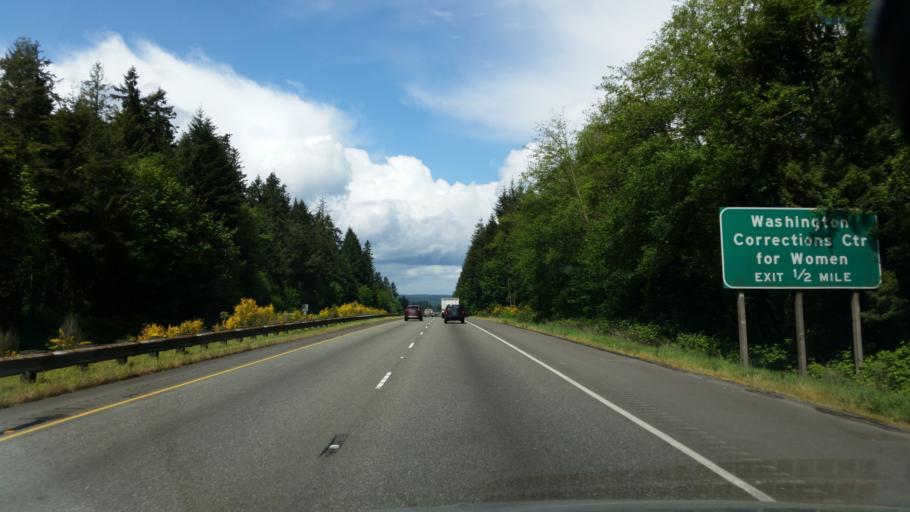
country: US
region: Washington
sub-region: Pierce County
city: Canterwood
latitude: 47.3480
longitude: -122.6102
